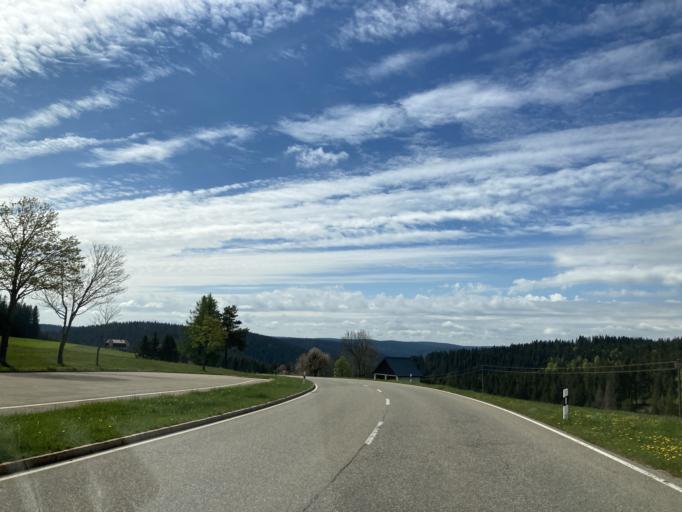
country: DE
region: Baden-Wuerttemberg
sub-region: Freiburg Region
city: Schonwald im Schwarzwald
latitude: 48.0882
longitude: 8.1978
